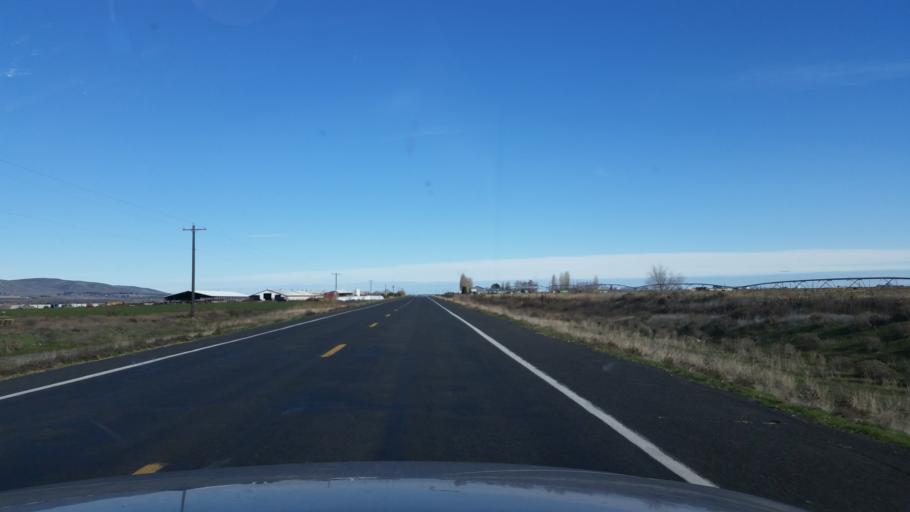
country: US
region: Washington
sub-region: Grant County
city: Ephrata
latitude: 47.2152
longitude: -119.6526
